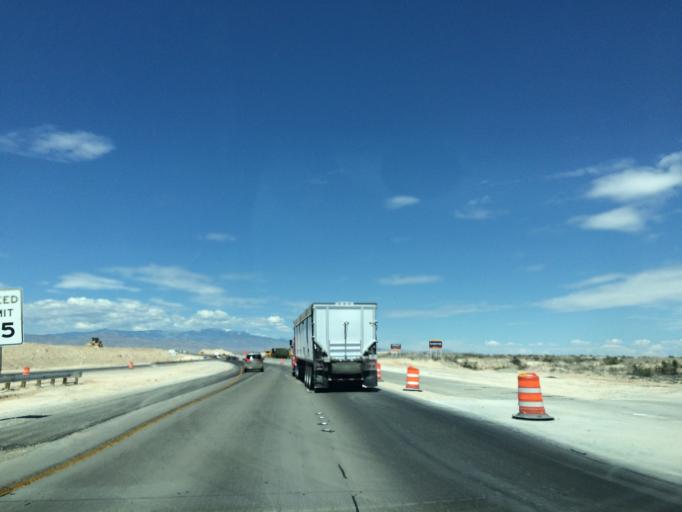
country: US
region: Nevada
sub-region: Clark County
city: Nellis Air Force Base
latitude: 36.2929
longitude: -115.1420
